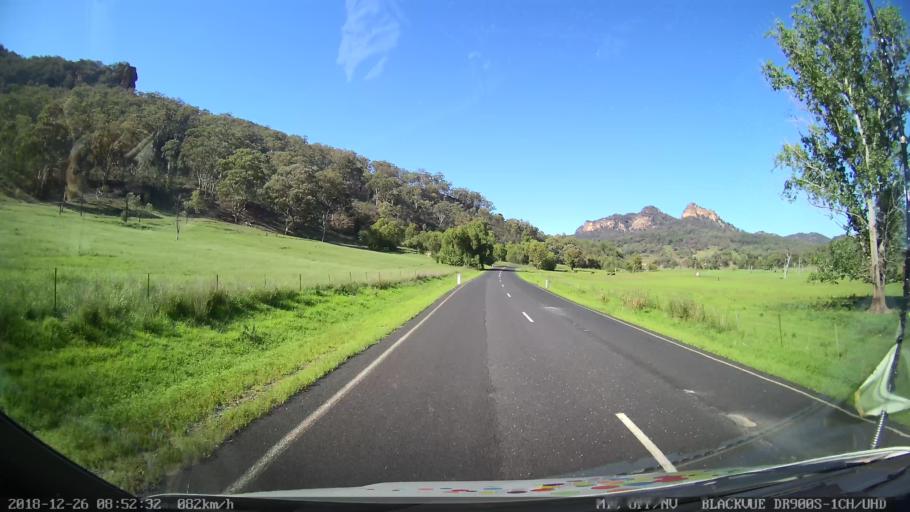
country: AU
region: New South Wales
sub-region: Mid-Western Regional
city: Kandos
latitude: -32.5977
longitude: 150.0857
